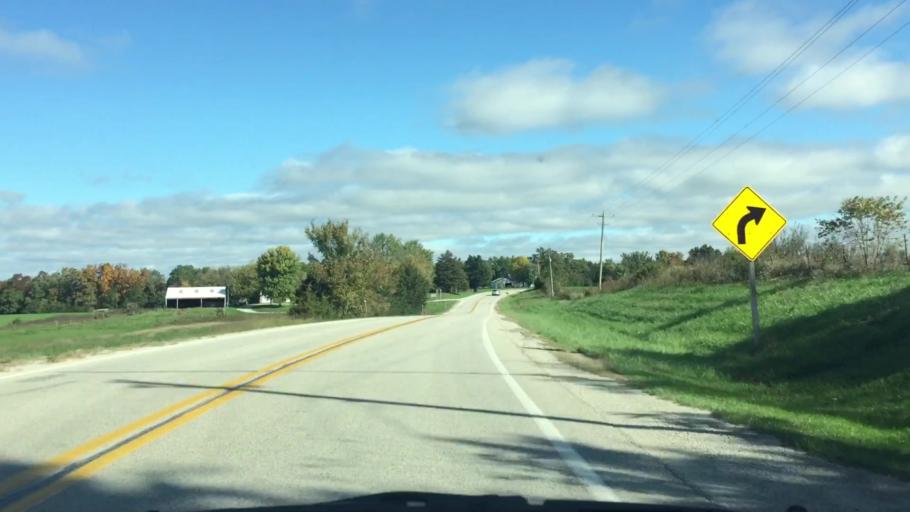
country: US
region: Iowa
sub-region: Decatur County
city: Leon
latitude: 40.6969
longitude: -93.7741
